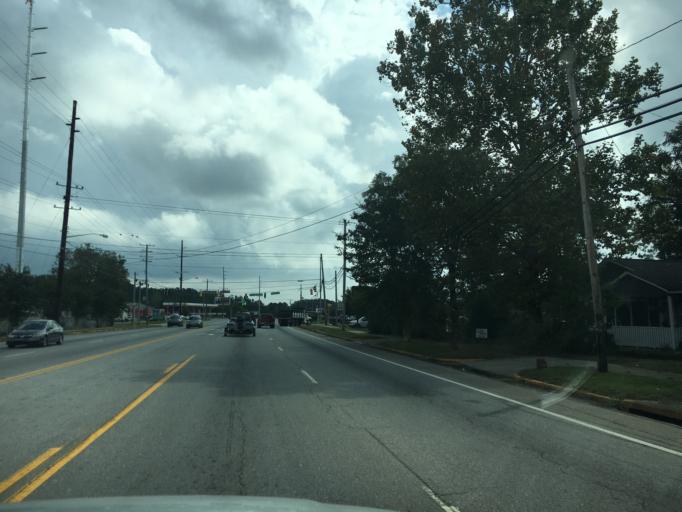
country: US
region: Georgia
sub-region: Elbert County
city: Elberton
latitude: 34.1017
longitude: -82.8503
